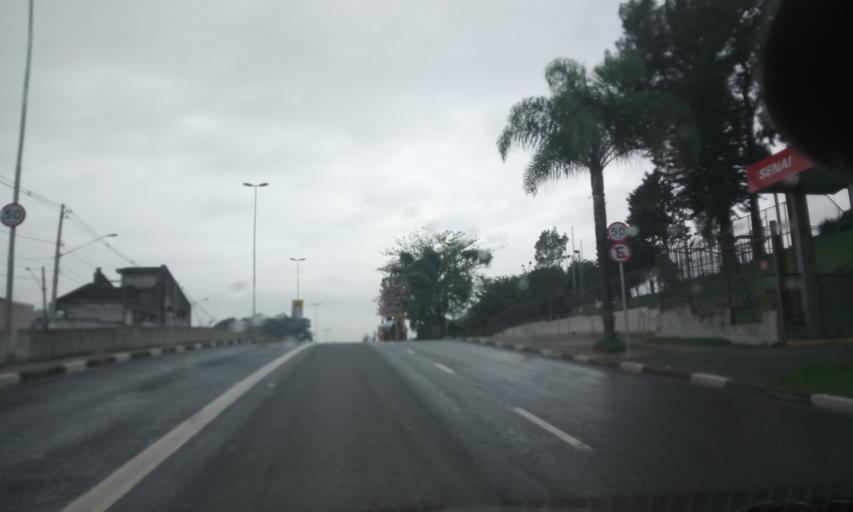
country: BR
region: Sao Paulo
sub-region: Sao Bernardo Do Campo
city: Sao Bernardo do Campo
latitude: -23.7118
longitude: -46.5769
